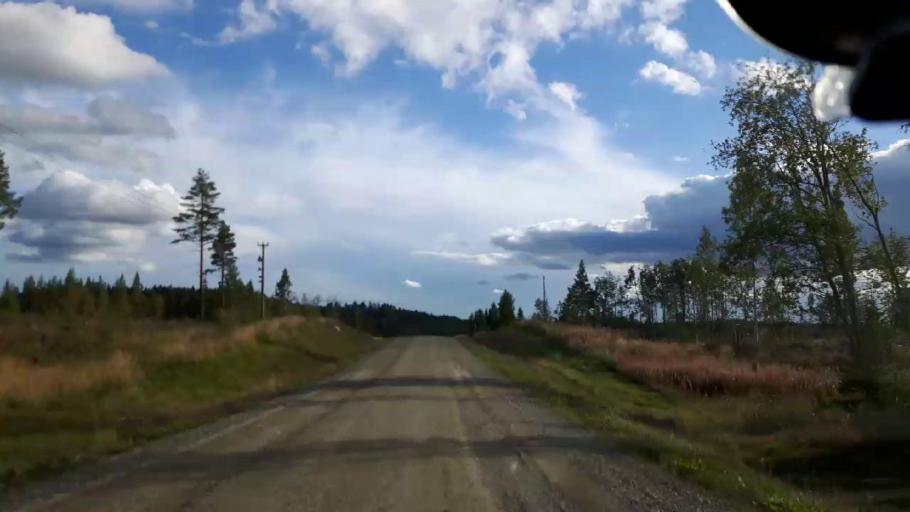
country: SE
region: Jaemtland
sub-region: Stroemsunds Kommun
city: Stroemsund
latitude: 63.3078
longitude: 15.6006
